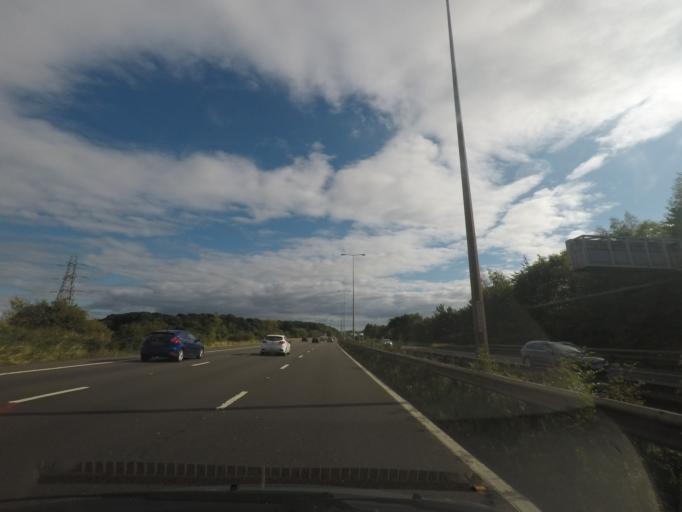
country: GB
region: England
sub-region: Leicestershire
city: Shepshed
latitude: 52.7725
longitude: -1.2767
